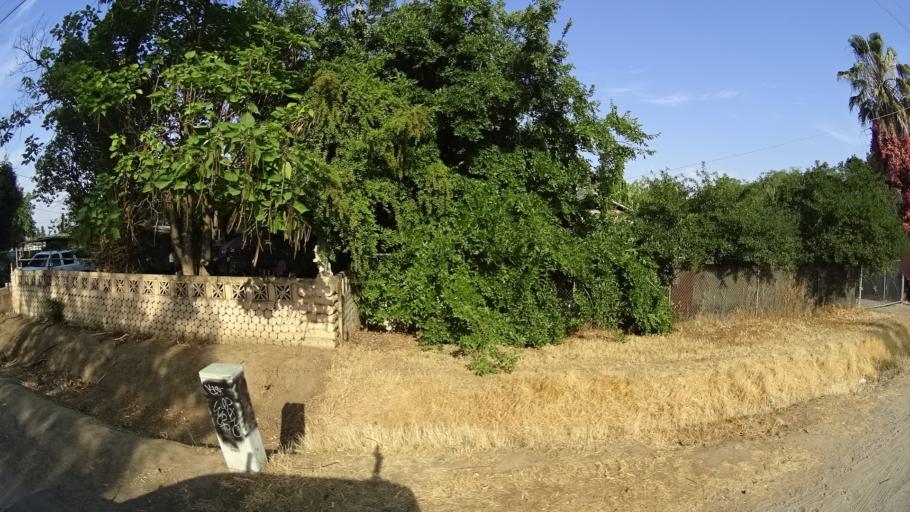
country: US
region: California
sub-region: Fresno County
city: West Park
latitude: 36.7516
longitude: -119.8532
